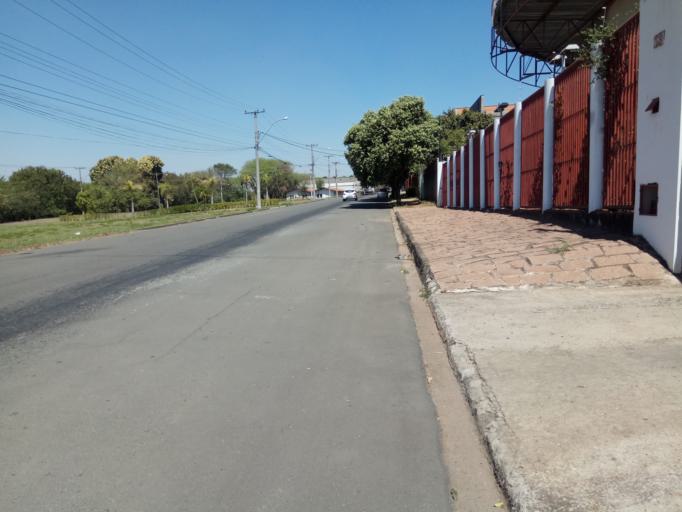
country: BR
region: Sao Paulo
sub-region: Piracicaba
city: Piracicaba
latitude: -22.7315
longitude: -47.5939
